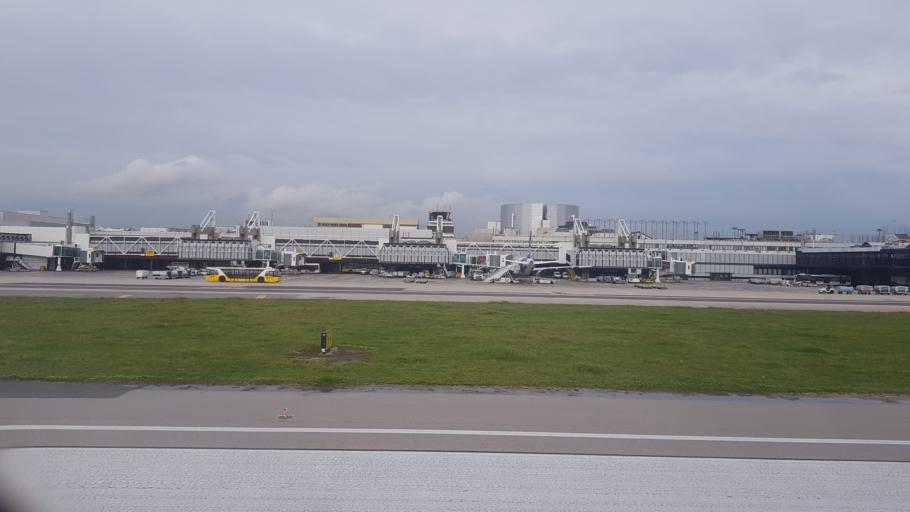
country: PT
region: Lisbon
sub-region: Loures
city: Moscavide
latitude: 38.7693
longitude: -9.1327
